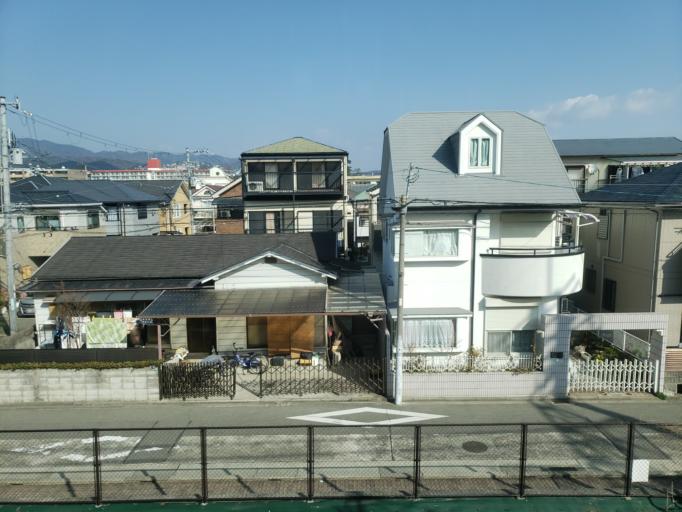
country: JP
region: Hyogo
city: Nishinomiya-hama
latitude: 34.7392
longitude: 135.3354
